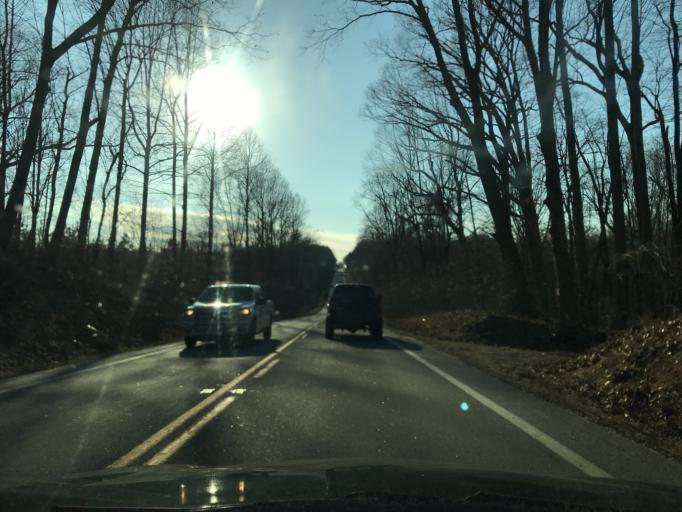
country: US
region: Virginia
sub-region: Prince Edward County
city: Farmville
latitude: 37.2735
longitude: -78.2709
